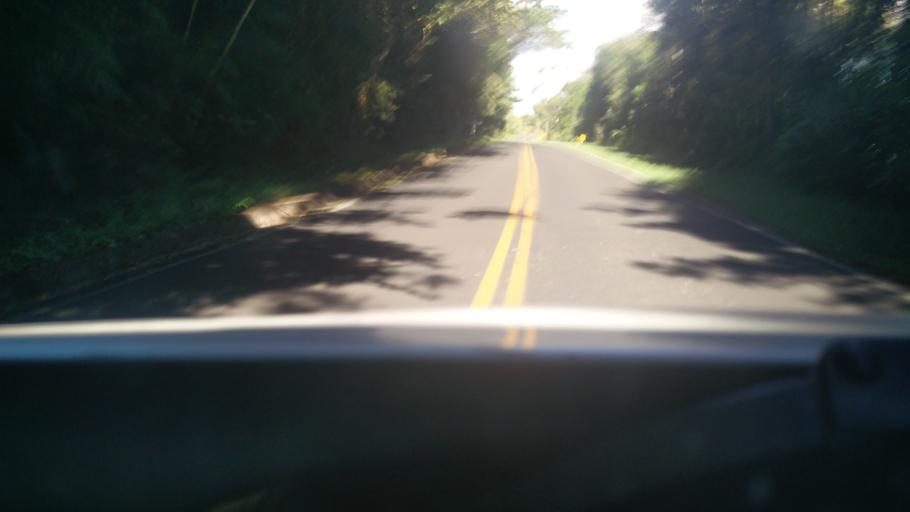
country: BR
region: Parana
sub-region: Palmeira
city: Palmeira
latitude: -25.4563
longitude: -49.8072
